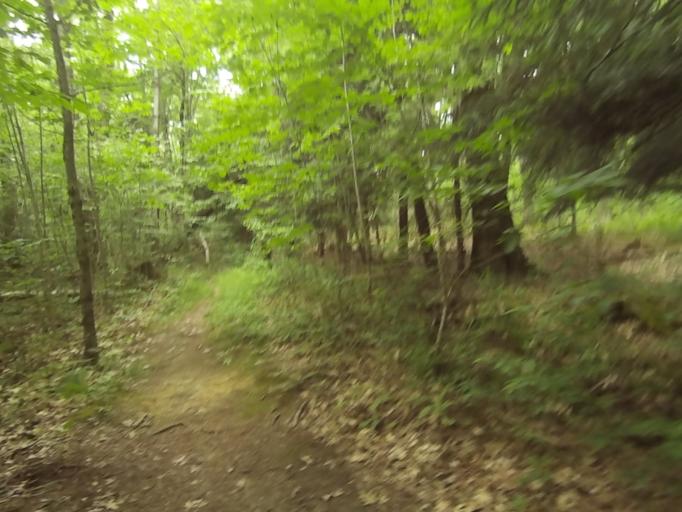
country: US
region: Pennsylvania
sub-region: Centre County
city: Stormstown
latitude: 40.9167
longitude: -78.0672
